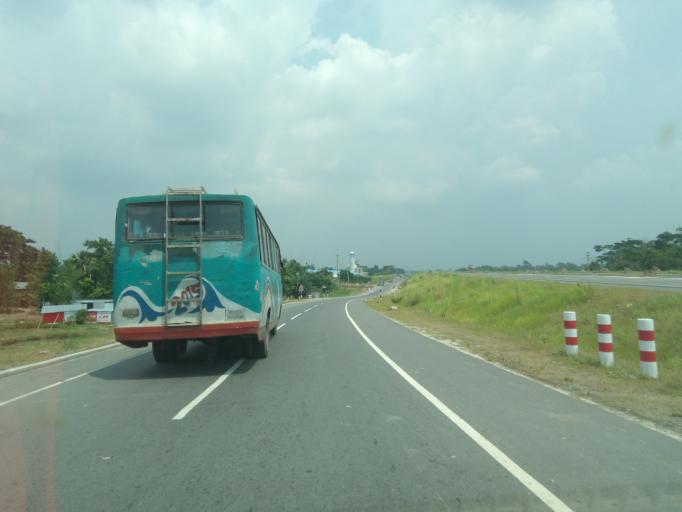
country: BD
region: Dhaka
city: Char Bhadrasan
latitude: 23.3996
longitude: 90.2149
